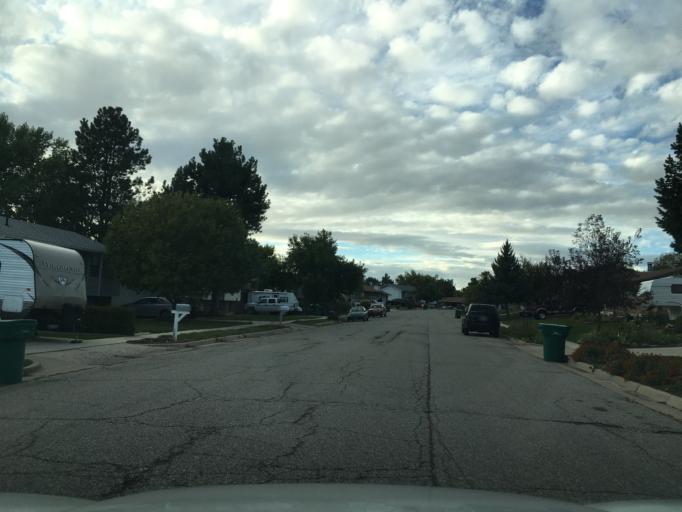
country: US
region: Utah
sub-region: Davis County
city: Layton
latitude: 41.0816
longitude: -111.9989
